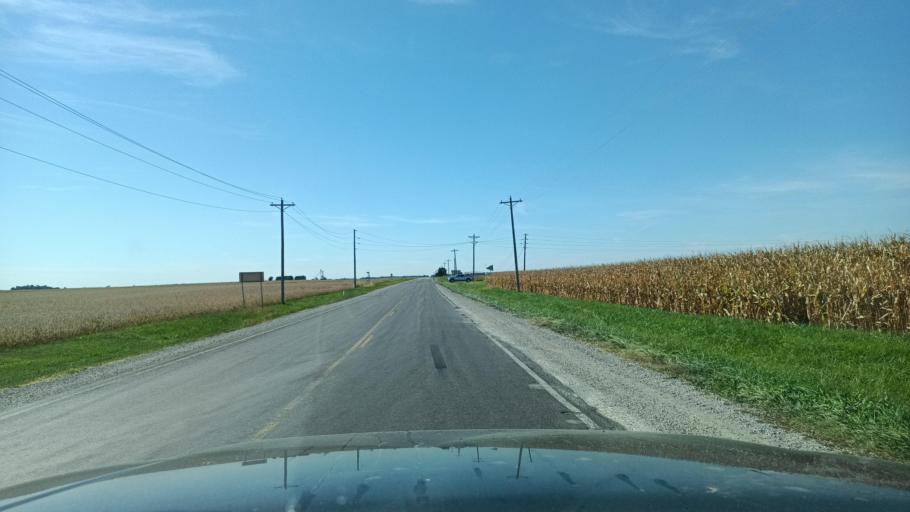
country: US
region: Illinois
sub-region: De Witt County
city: Farmer City
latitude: 40.2238
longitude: -88.7445
